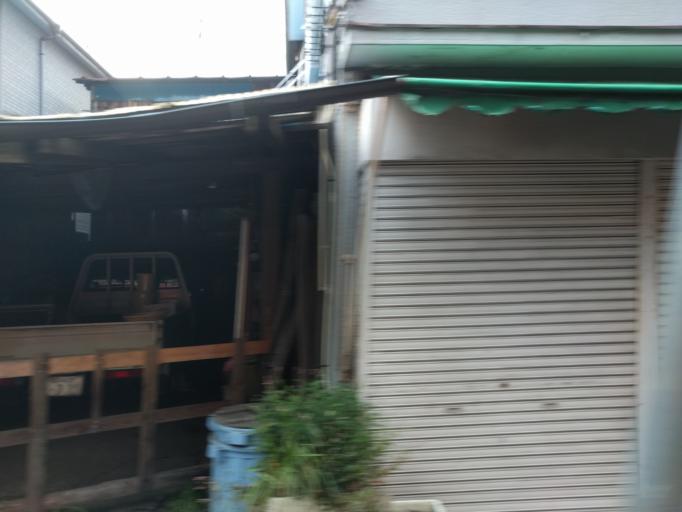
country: JP
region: Tokyo
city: Tokyo
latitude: 35.6798
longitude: 139.6726
